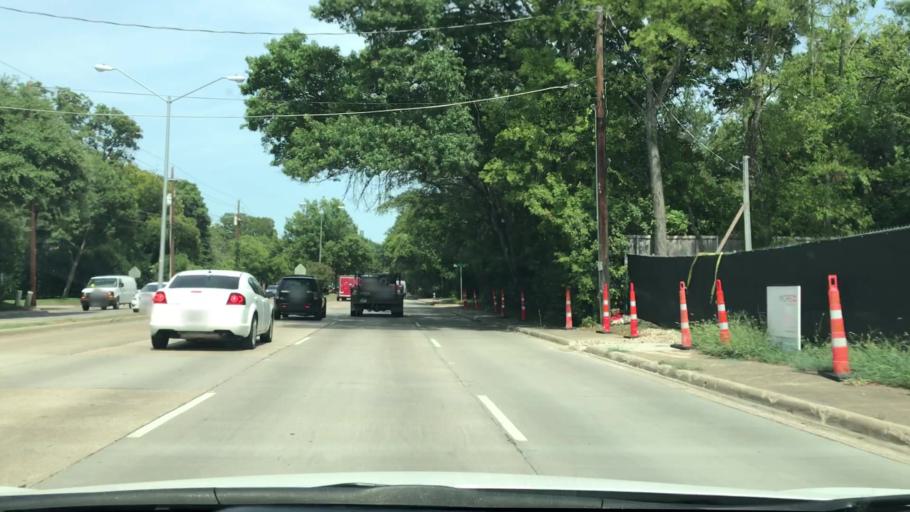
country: US
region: Texas
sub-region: Dallas County
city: University Park
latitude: 32.8800
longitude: -96.8073
